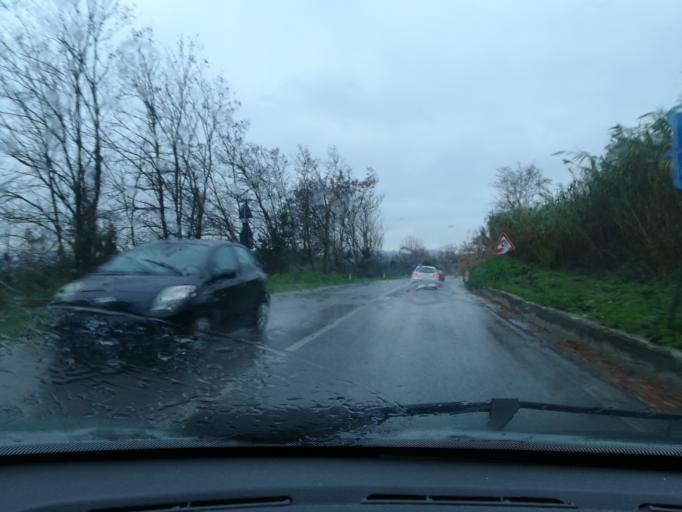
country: IT
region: The Marches
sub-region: Provincia di Macerata
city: Sforzacosta
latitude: 43.2768
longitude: 13.4312
